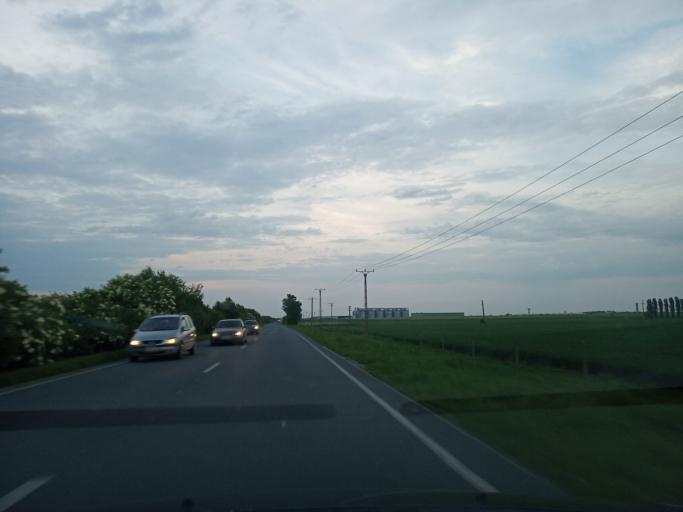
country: RO
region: Timis
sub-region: Comuna Voiteg
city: Voiteg
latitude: 45.4336
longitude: 21.2312
